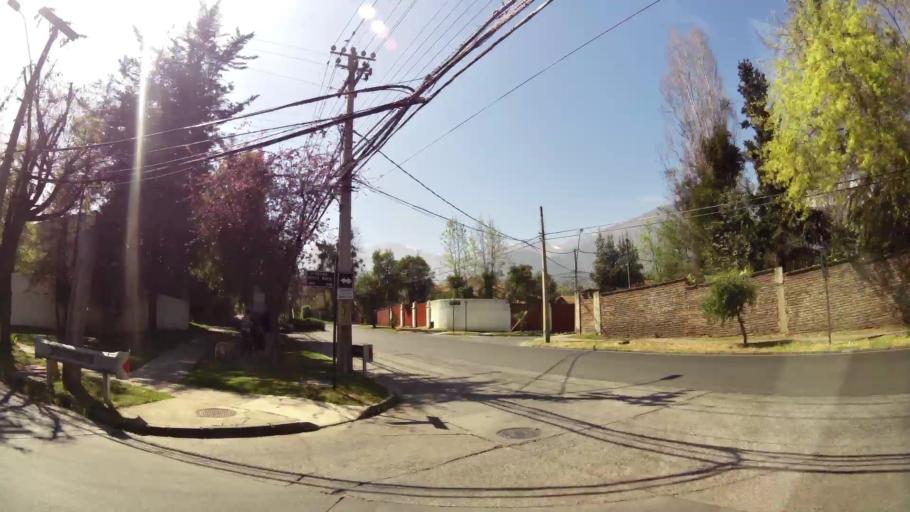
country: CL
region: Santiago Metropolitan
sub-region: Provincia de Santiago
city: Villa Presidente Frei, Nunoa, Santiago, Chile
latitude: -33.4385
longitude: -70.5299
